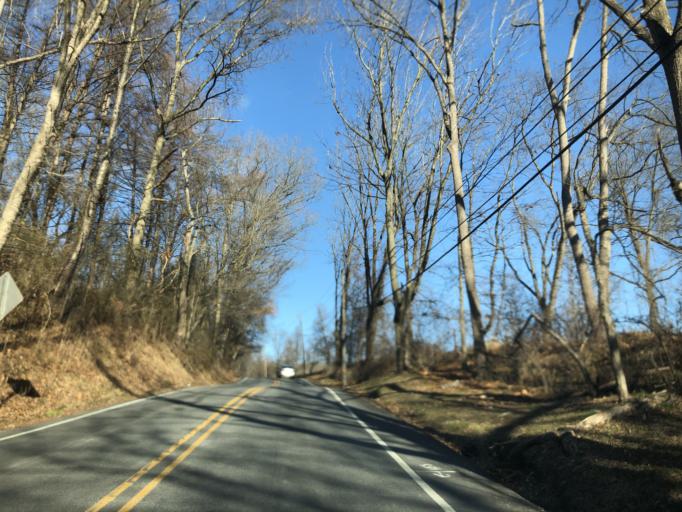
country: US
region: Pennsylvania
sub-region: Chester County
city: South Coatesville
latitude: 39.9329
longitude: -75.8306
